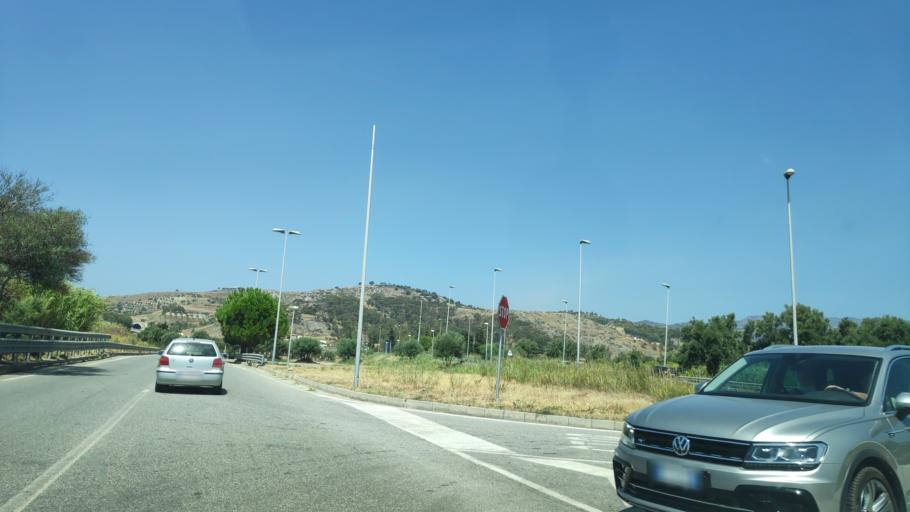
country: IT
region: Calabria
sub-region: Provincia di Reggio Calabria
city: Palizzi Marina
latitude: 37.9223
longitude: 15.9553
